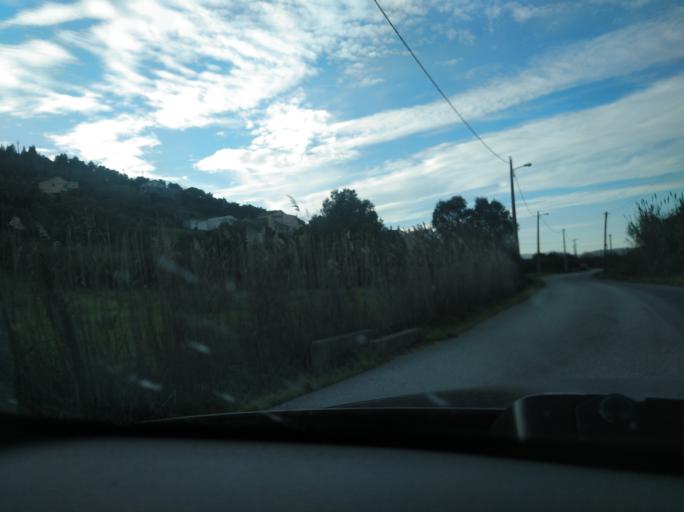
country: PT
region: Lisbon
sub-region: Loures
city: Unhos
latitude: 38.8352
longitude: -9.1231
